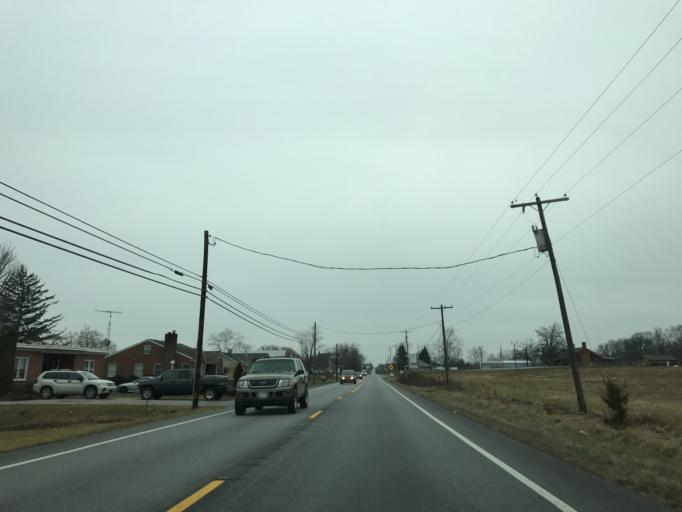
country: US
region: Maryland
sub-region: Carroll County
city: Taneytown
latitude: 39.6666
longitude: -77.1905
